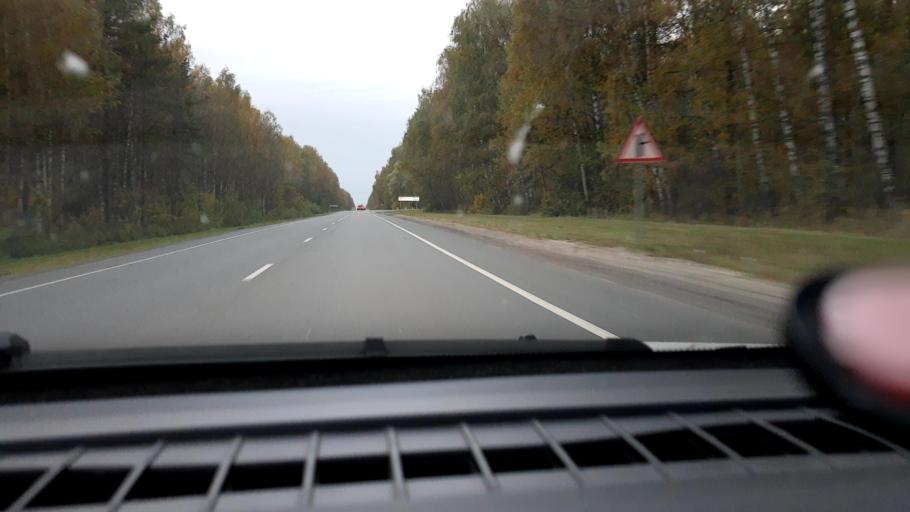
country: RU
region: Vladimir
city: Orgtrud
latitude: 56.2099
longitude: 40.6328
